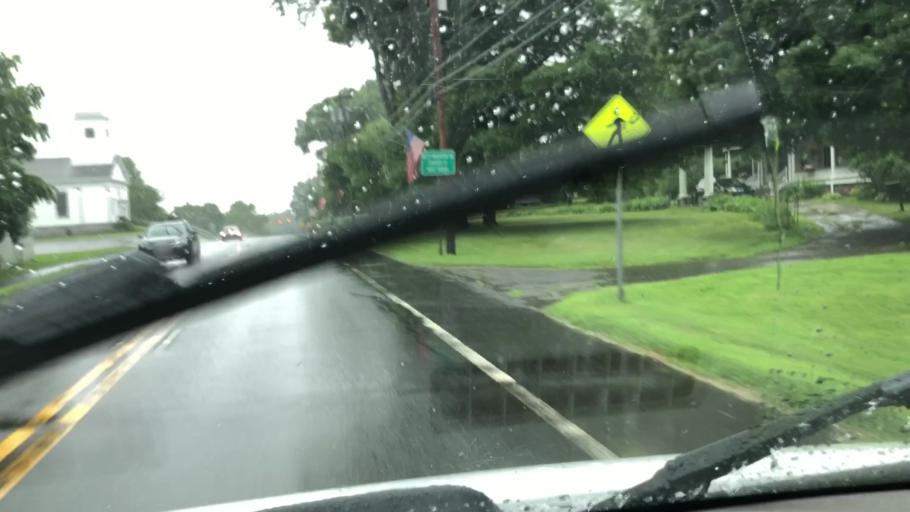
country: US
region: Massachusetts
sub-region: Berkshire County
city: Adams
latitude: 42.5638
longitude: -73.1646
